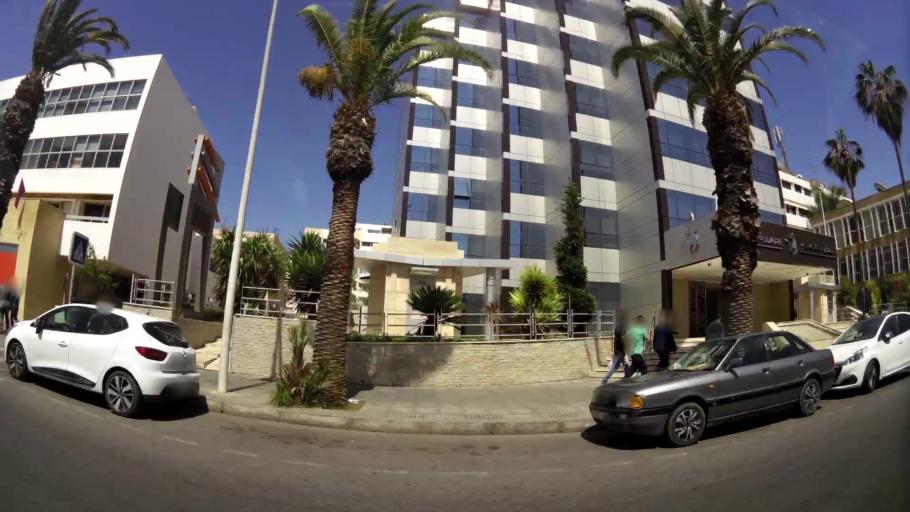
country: MA
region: Souss-Massa-Draa
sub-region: Agadir-Ida-ou-Tnan
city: Agadir
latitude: 30.4163
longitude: -9.5954
